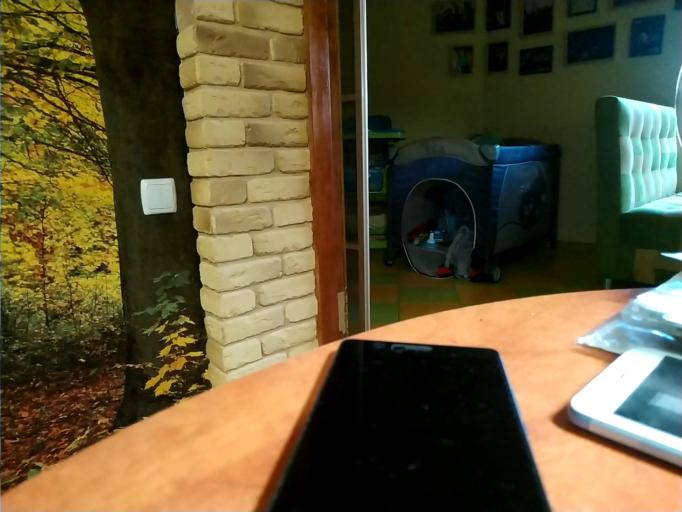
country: RU
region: Orjol
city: Znamenskoye
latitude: 53.5466
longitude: 35.4897
